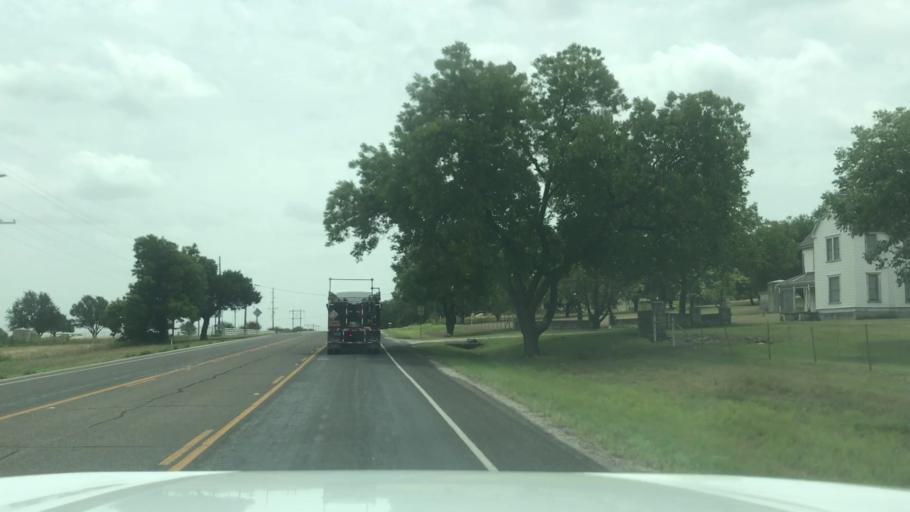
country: US
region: Texas
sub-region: Bosque County
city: Clifton
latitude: 31.7699
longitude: -97.5696
